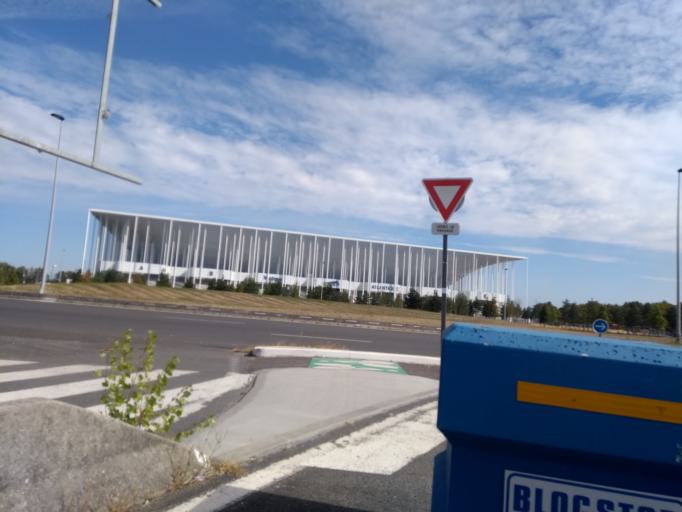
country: FR
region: Aquitaine
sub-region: Departement de la Gironde
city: Le Bouscat
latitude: 44.8978
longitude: -0.5662
